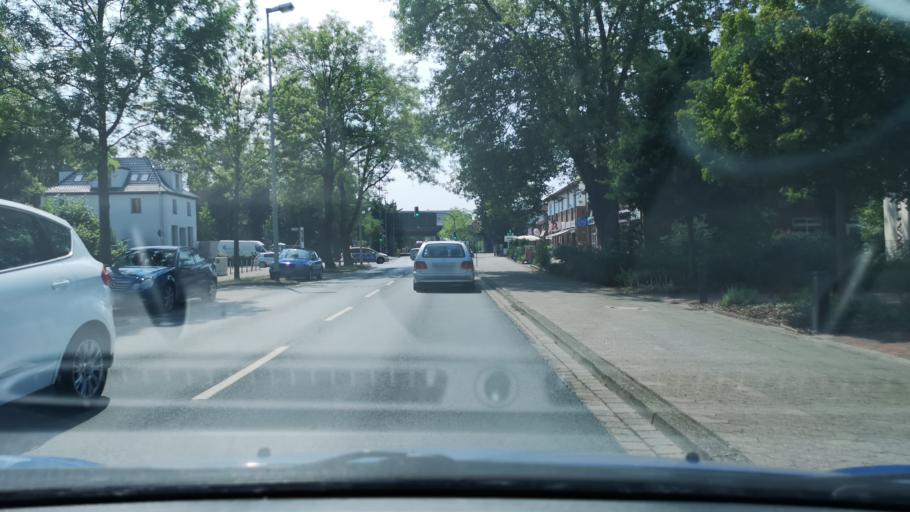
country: DE
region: Lower Saxony
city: Isernhagen Farster Bauerschaft
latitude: 52.4327
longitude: 9.8019
